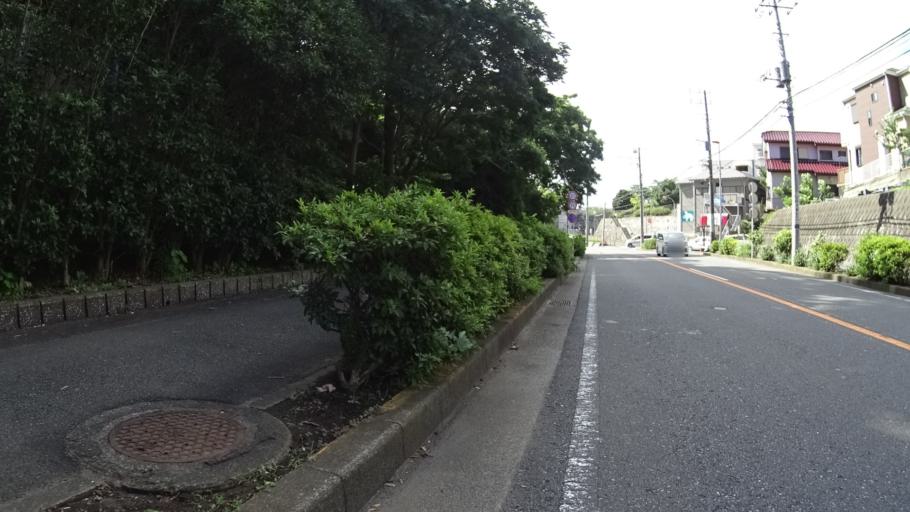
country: JP
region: Kanagawa
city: Yokosuka
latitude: 35.2575
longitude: 139.7082
